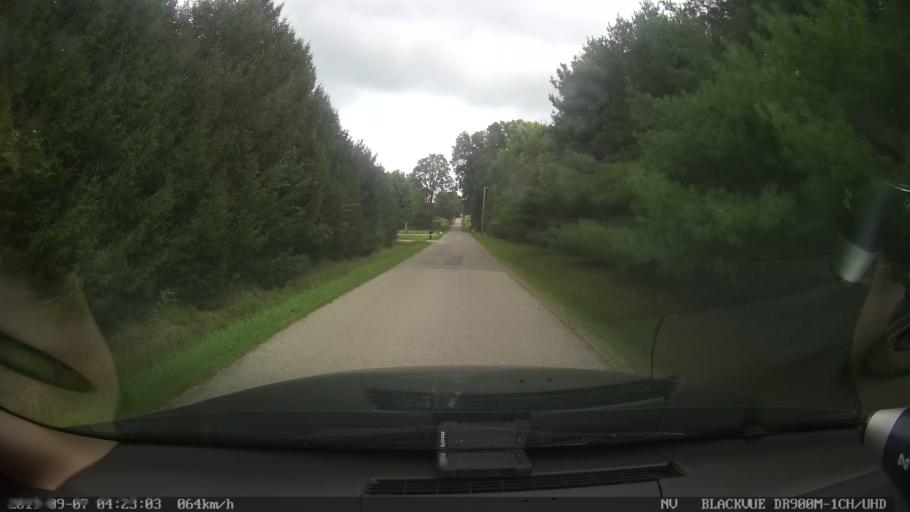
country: US
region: Ohio
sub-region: Knox County
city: Centerburg
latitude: 40.2767
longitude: -82.6711
